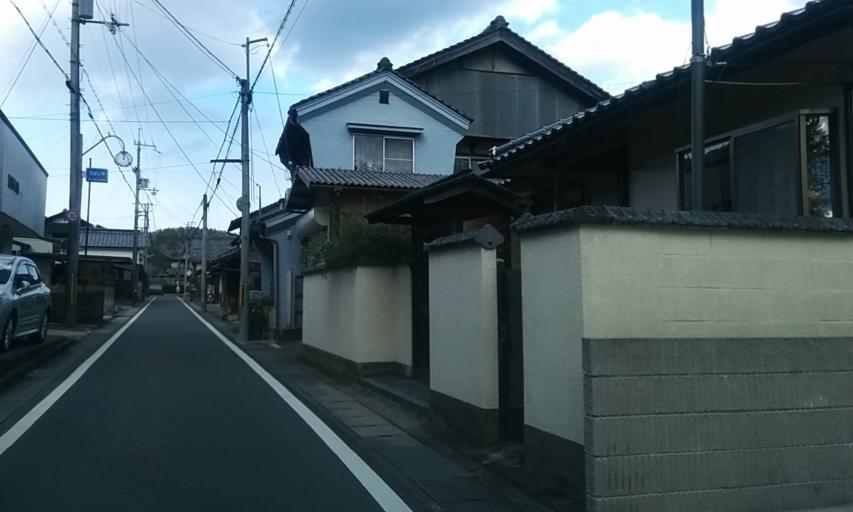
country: JP
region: Kyoto
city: Ayabe
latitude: 35.3421
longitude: 135.3102
